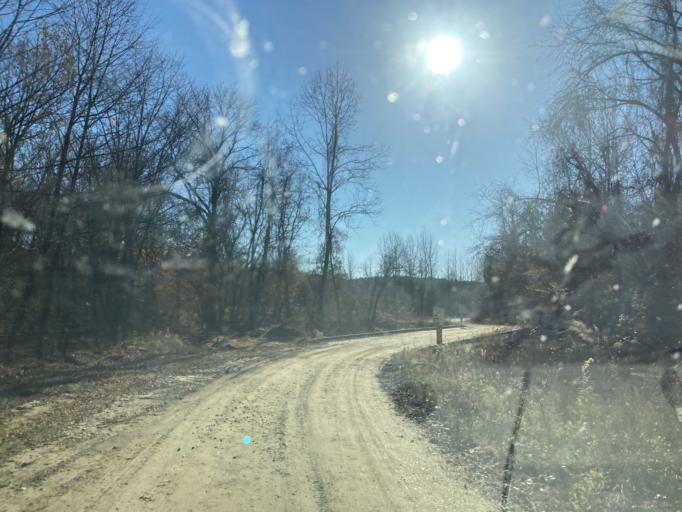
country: US
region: Mississippi
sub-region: Yazoo County
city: Yazoo City
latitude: 32.7067
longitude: -90.4719
